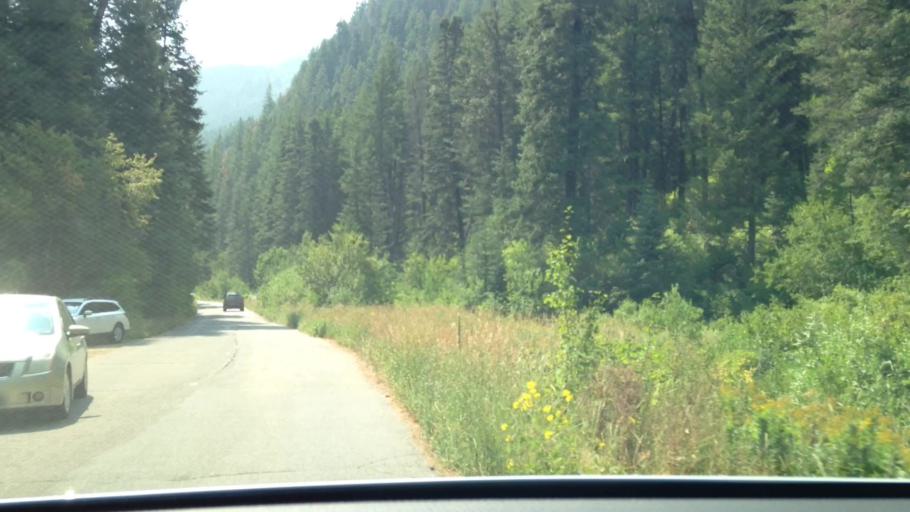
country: US
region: Utah
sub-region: Summit County
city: Summit Park
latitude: 40.7053
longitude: -111.6898
